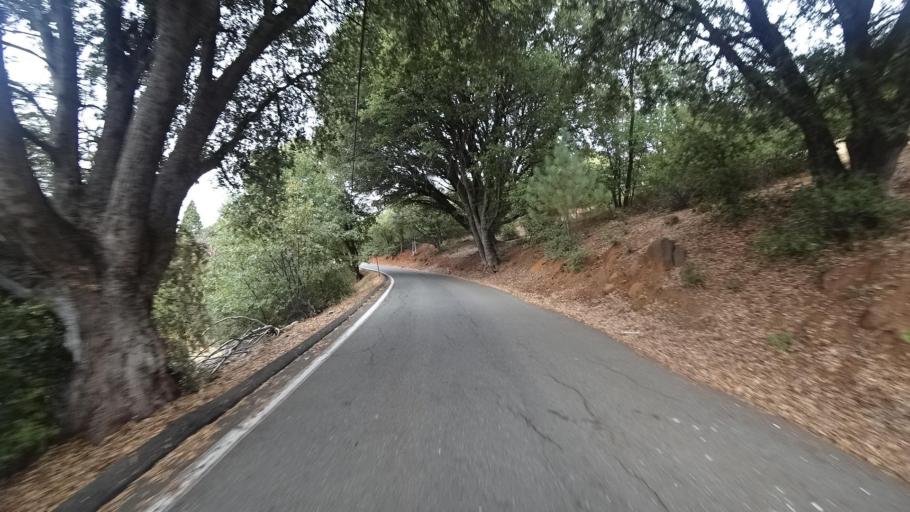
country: US
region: California
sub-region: San Diego County
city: Julian
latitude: 32.9946
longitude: -116.5869
